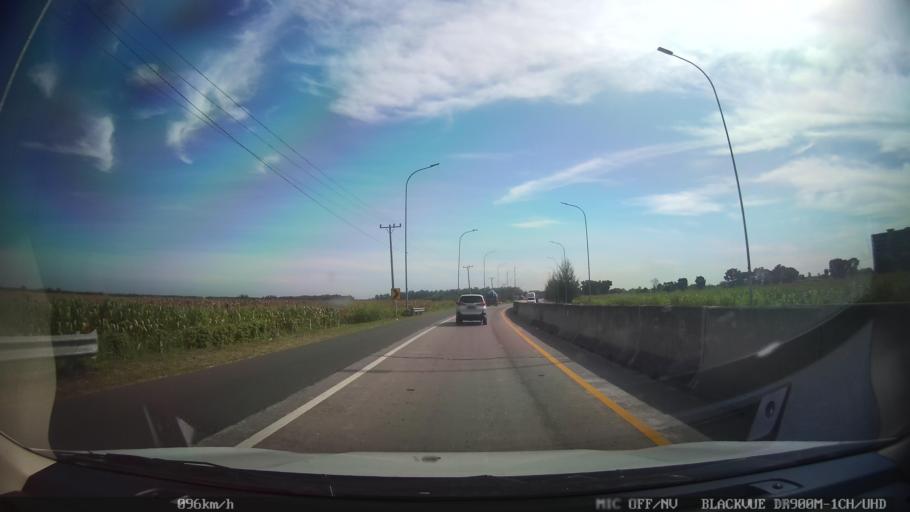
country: ID
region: North Sumatra
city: Sunggal
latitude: 3.6272
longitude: 98.6283
